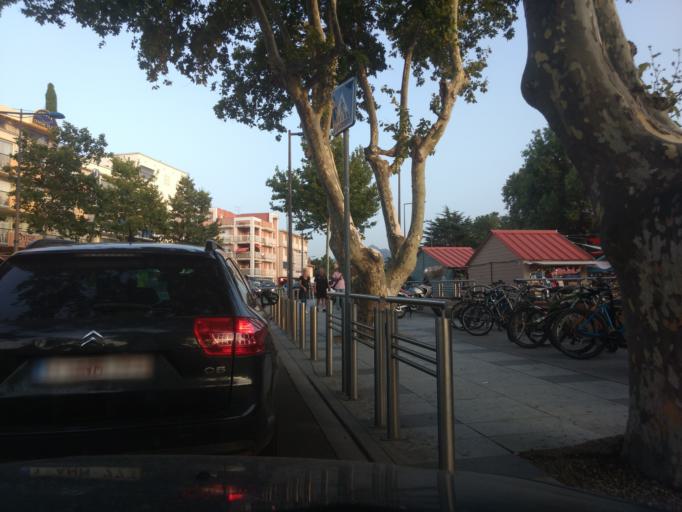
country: FR
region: Languedoc-Roussillon
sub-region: Departement des Pyrenees-Orientales
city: Argelers
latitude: 42.5516
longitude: 3.0463
